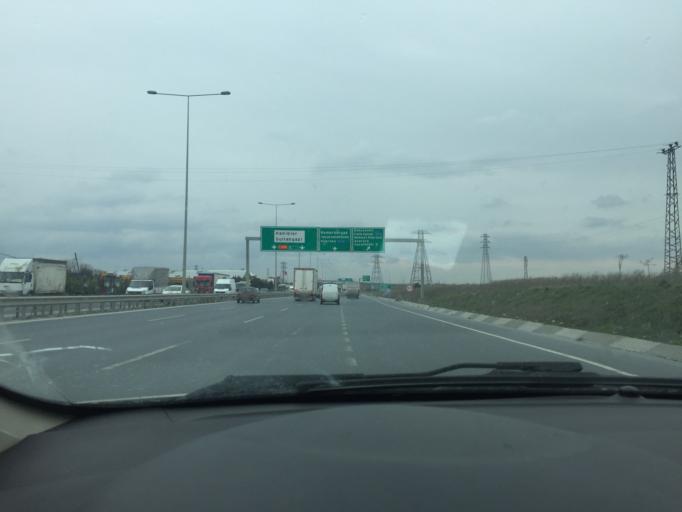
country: TR
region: Istanbul
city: Basaksehir
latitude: 41.1427
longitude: 28.7993
